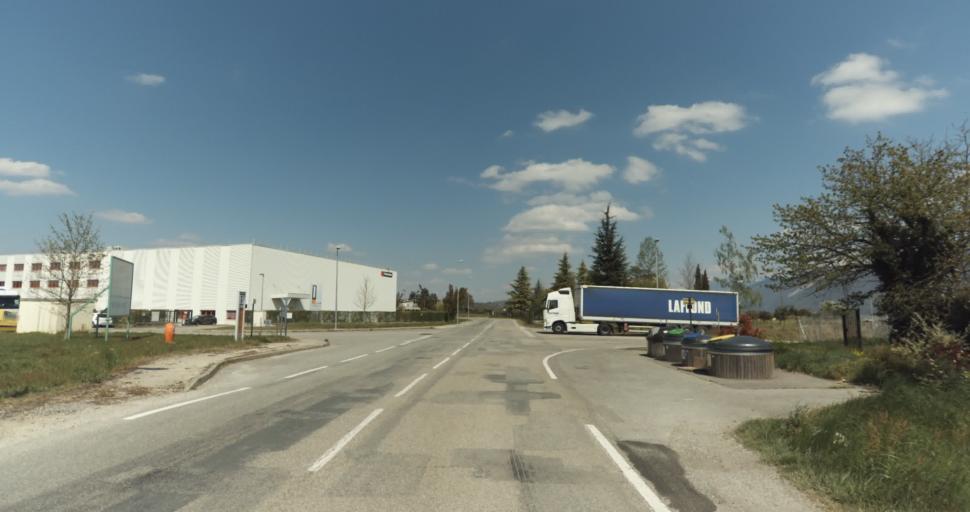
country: FR
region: Rhone-Alpes
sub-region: Departement de l'Isere
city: Saint-Marcellin
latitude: 45.1378
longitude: 5.3223
